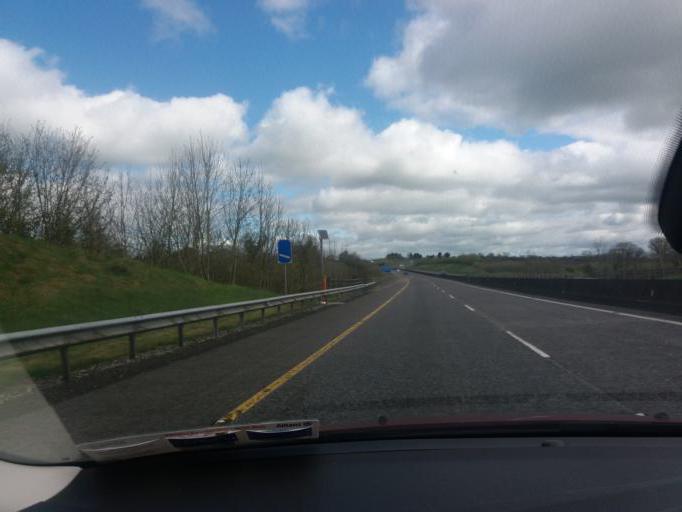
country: IE
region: Munster
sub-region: County Cork
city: Rathcormac
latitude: 52.0480
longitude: -8.3093
